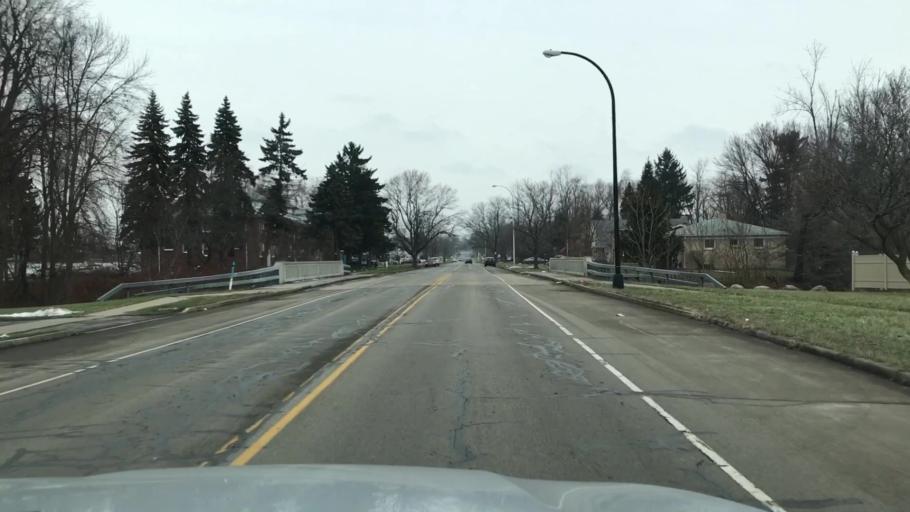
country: US
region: New York
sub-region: Erie County
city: Lackawanna
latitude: 42.8202
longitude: -78.8101
